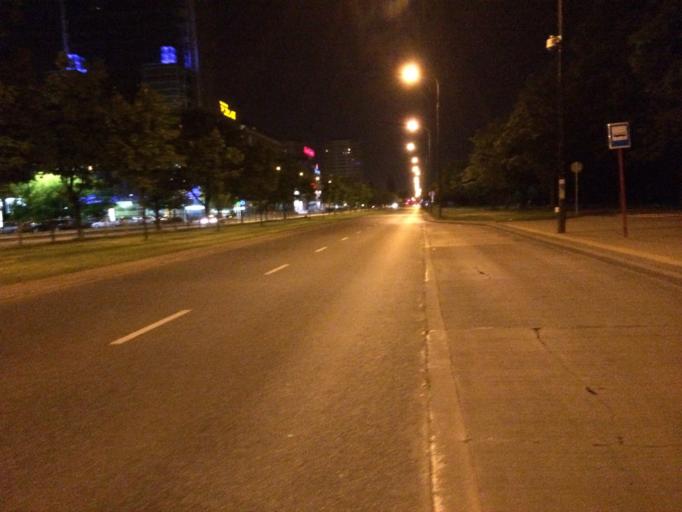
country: PL
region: Masovian Voivodeship
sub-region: Warszawa
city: Praga Poludnie
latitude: 52.2339
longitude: 21.1070
